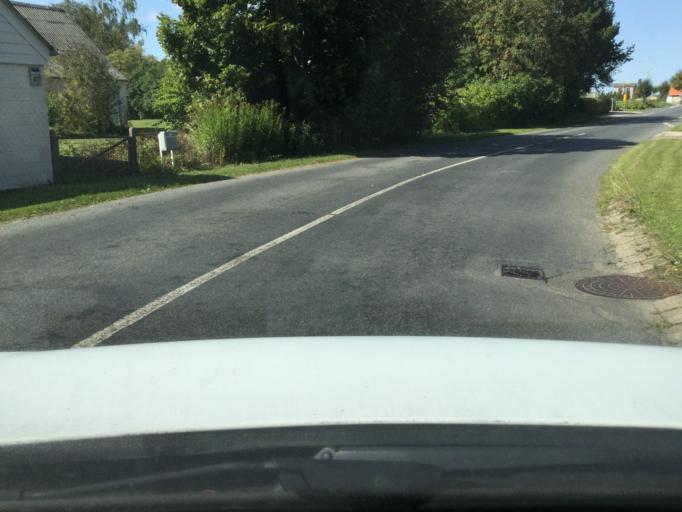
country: DK
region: Zealand
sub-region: Lolland Kommune
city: Rodby
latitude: 54.7093
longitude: 11.3848
